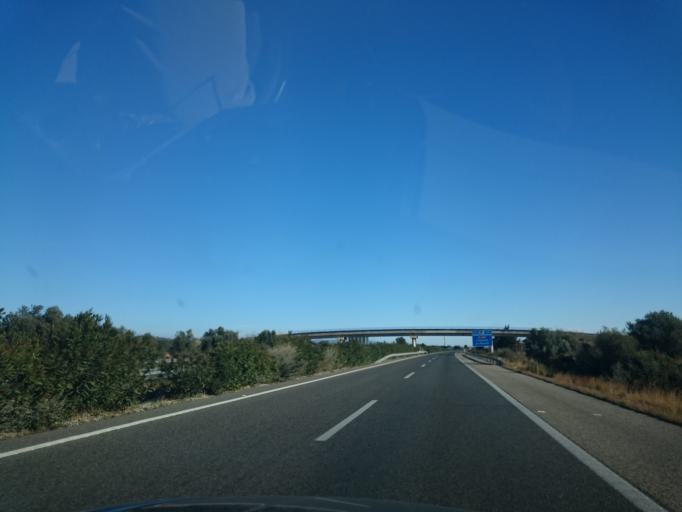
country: ES
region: Catalonia
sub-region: Provincia de Tarragona
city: Camarles
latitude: 40.7803
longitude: 0.6463
